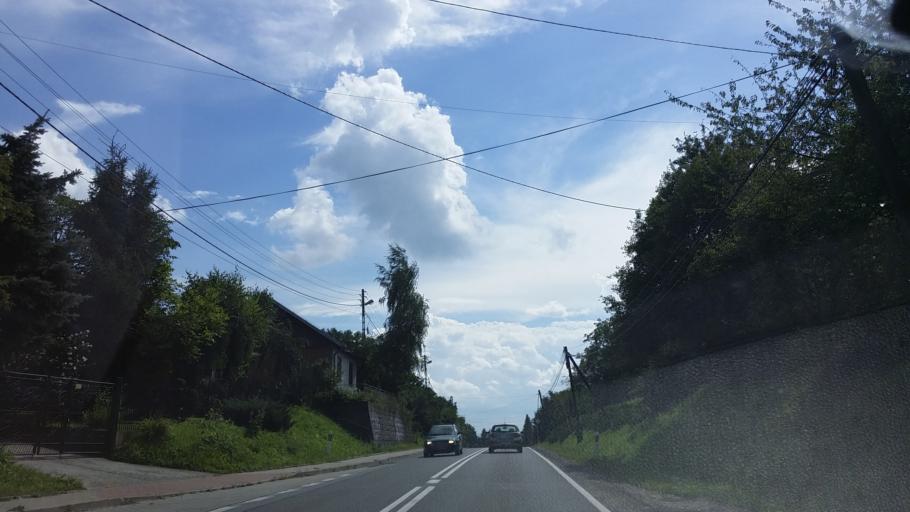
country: PL
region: Lesser Poland Voivodeship
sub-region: Powiat wielicki
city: Pawlikowice
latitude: 49.9673
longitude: 20.0584
